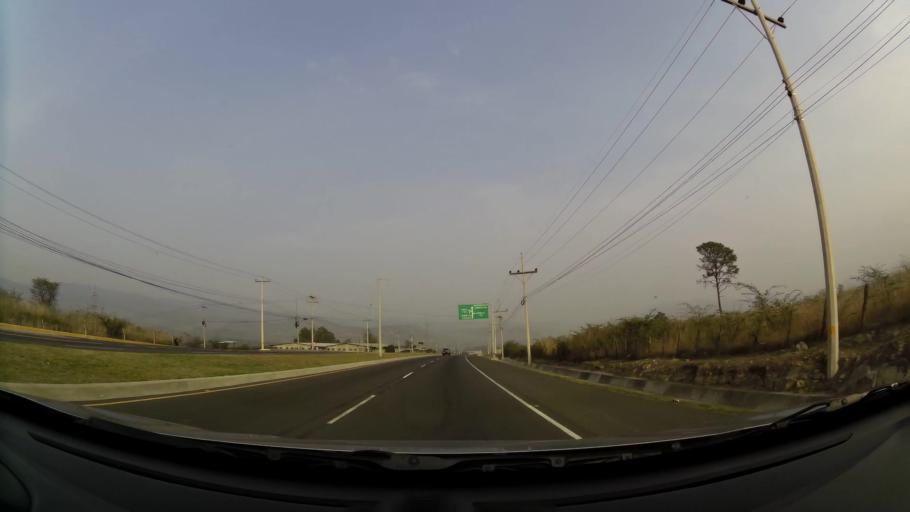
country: HN
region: Francisco Morazan
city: Tamara
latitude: 14.1974
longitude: -87.3383
